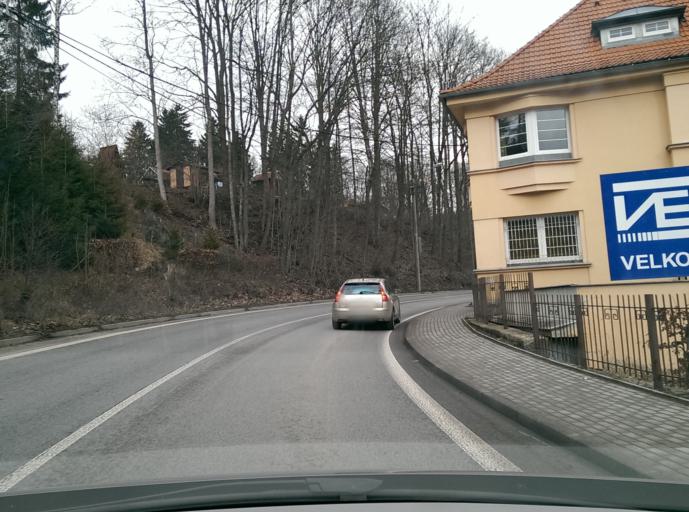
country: CZ
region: Liberecky
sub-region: Okres Jablonec nad Nisou
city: Jablonec nad Nisou
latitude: 50.7361
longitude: 15.1897
